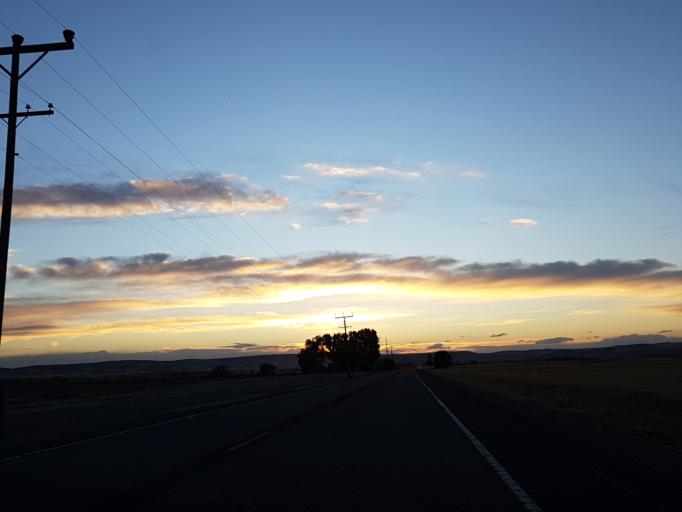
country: US
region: Oregon
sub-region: Malheur County
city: Vale
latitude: 43.9391
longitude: -117.3396
